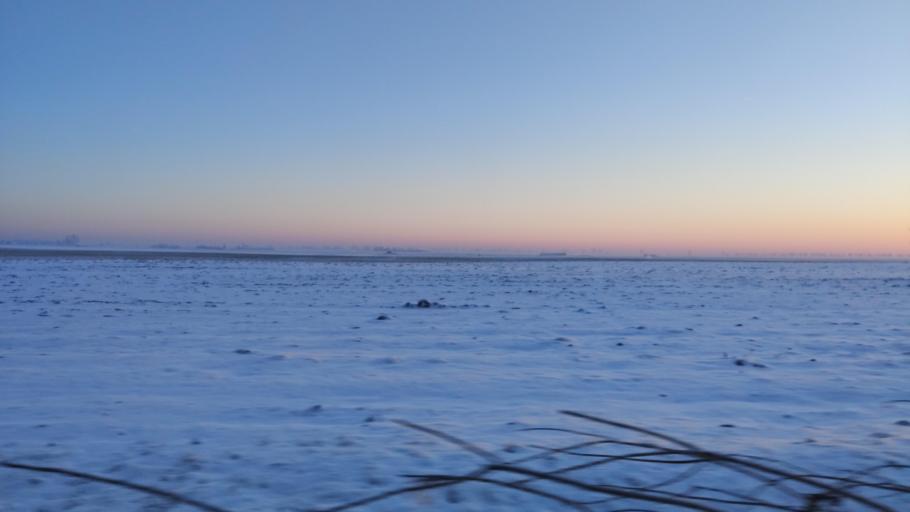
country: PL
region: Kujawsko-Pomorskie
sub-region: Powiat zninski
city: Znin
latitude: 52.8692
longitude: 17.8122
